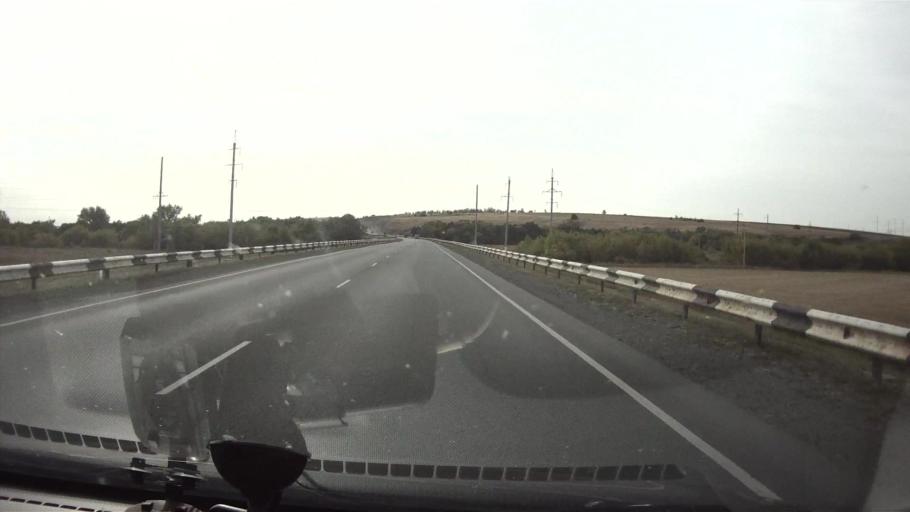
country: RU
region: Saratov
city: Sennoy
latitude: 52.1427
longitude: 46.8945
